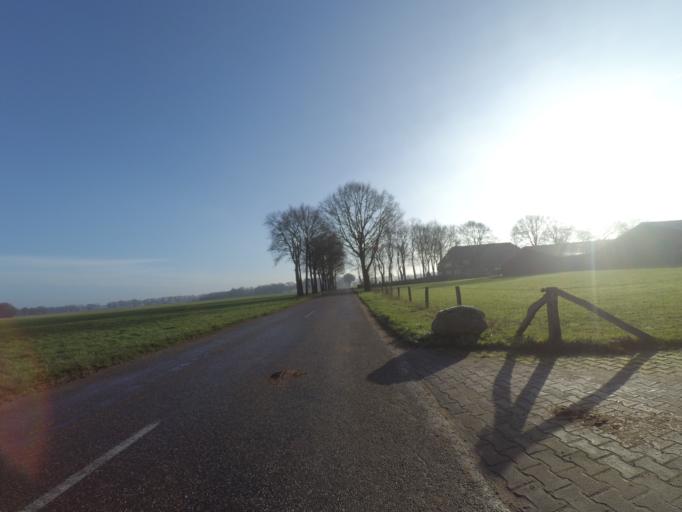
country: NL
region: Drenthe
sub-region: Gemeente Coevorden
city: Sleen
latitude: 52.8320
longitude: 6.6893
